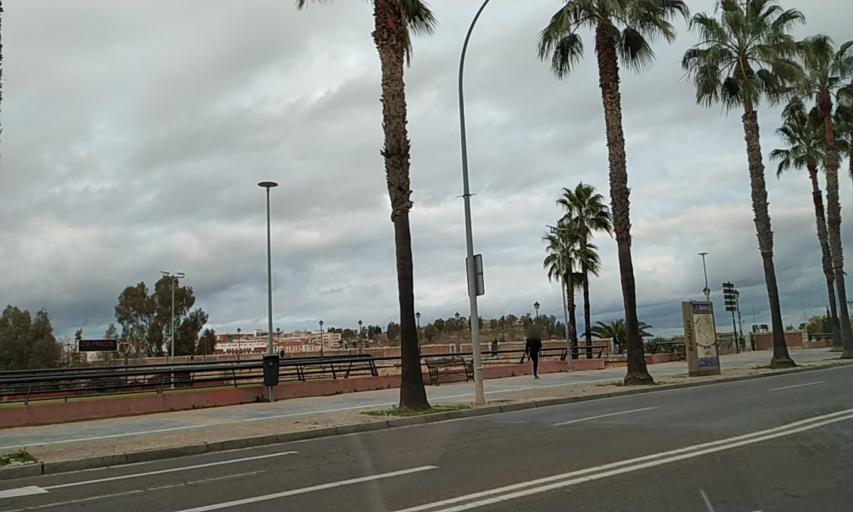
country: ES
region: Extremadura
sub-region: Provincia de Badajoz
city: Badajoz
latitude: 38.8806
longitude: -6.9763
